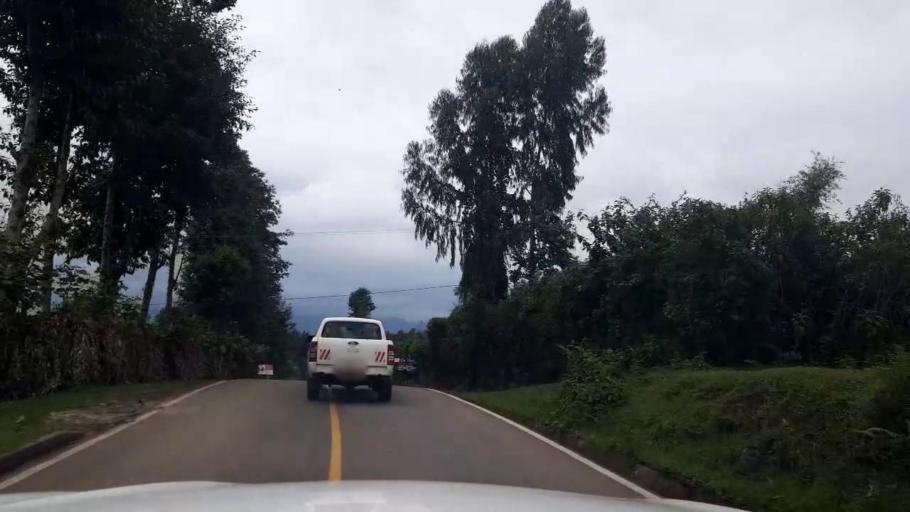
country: RW
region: Northern Province
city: Musanze
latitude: -1.4301
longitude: 29.5616
